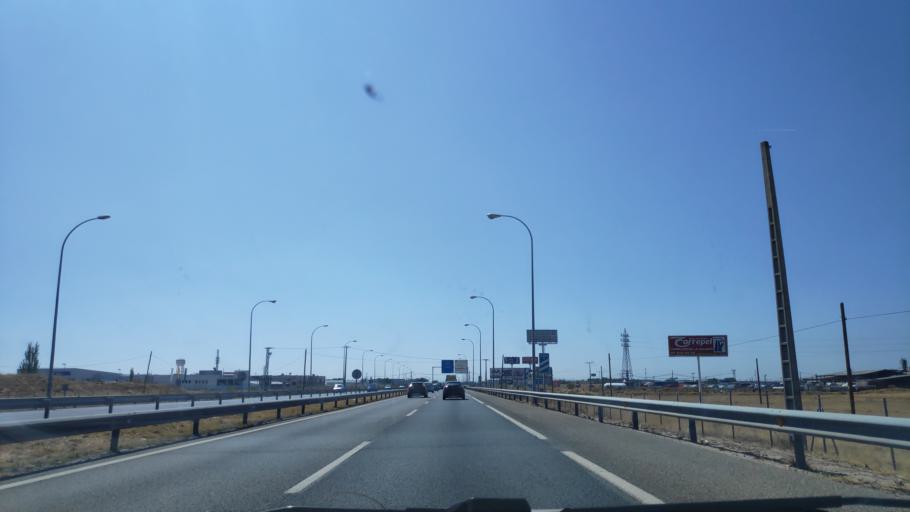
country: ES
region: Madrid
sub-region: Provincia de Madrid
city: Parla
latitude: 40.2310
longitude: -3.7832
